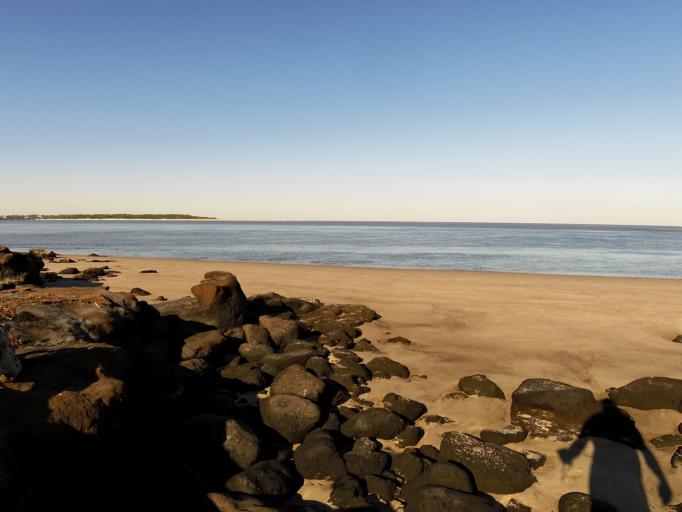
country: US
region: Florida
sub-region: Duval County
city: Atlantic Beach
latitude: 30.4992
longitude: -81.4433
